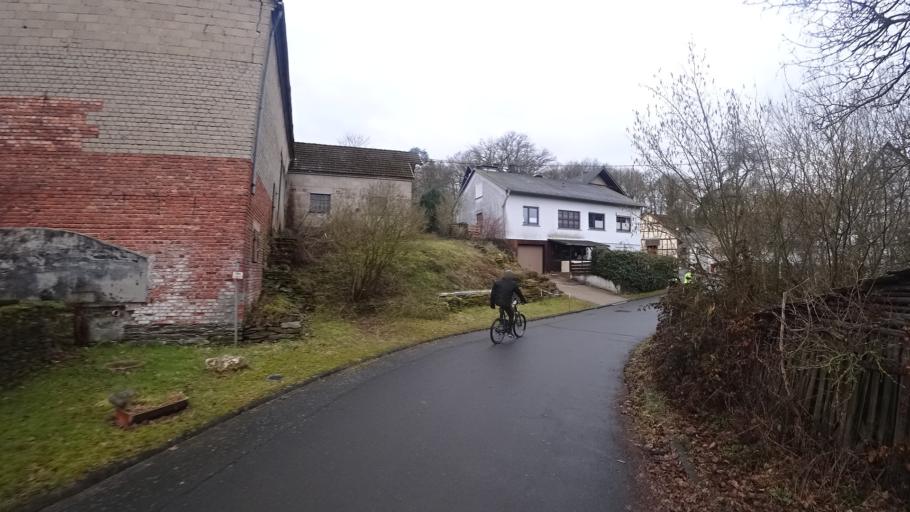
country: DE
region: Rheinland-Pfalz
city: Diethardt
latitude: 50.1620
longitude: 7.8715
